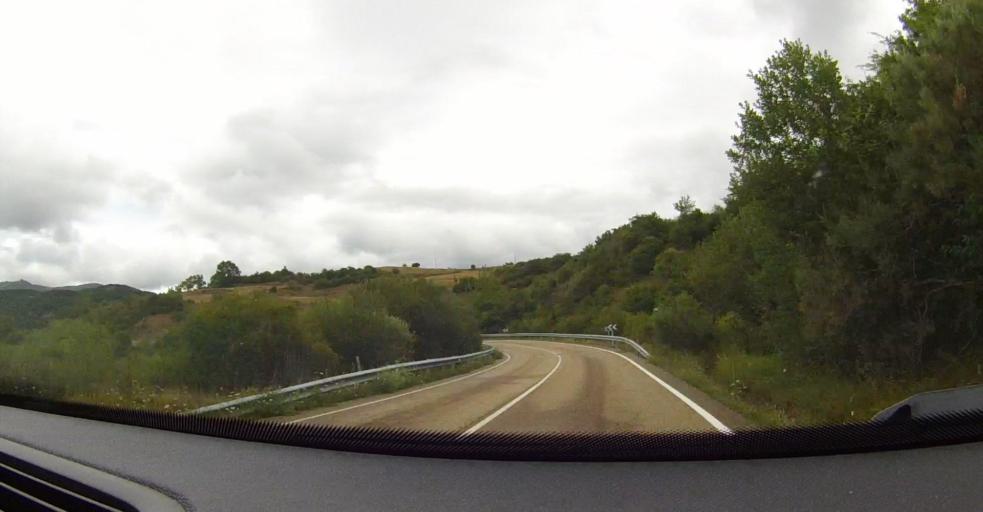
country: ES
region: Castille and Leon
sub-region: Provincia de Leon
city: Reyero
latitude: 42.9413
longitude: -5.2620
